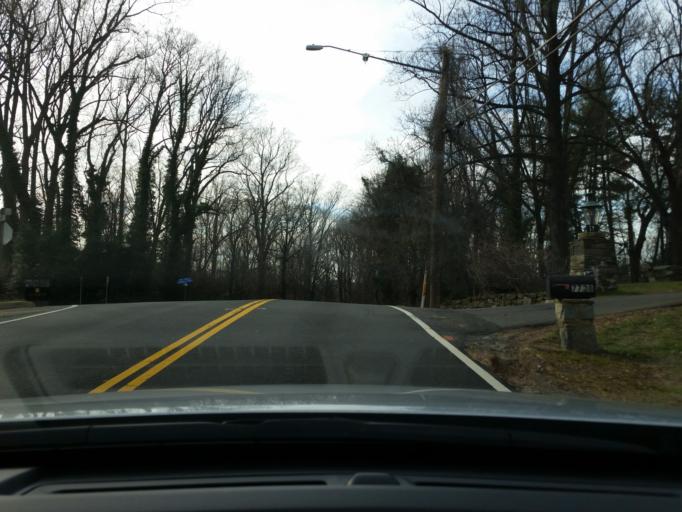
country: US
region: Virginia
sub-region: Fairfax County
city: McLean
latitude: 38.9597
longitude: -77.2129
